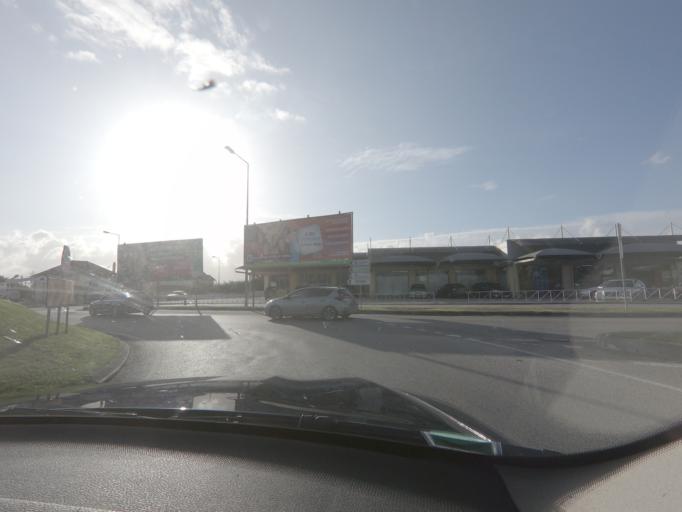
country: PT
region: Viseu
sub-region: Concelho de Tondela
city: Tondela
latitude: 40.5276
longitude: -8.0889
